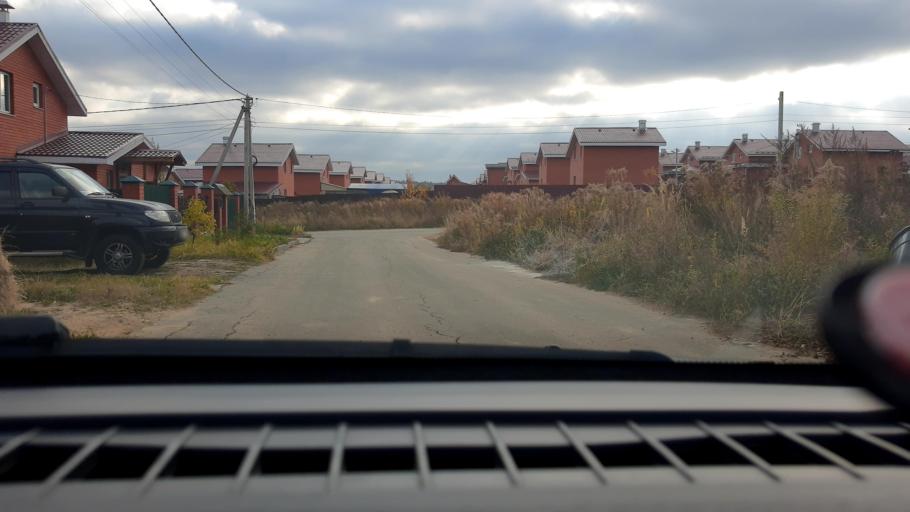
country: RU
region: Nizjnij Novgorod
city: Afonino
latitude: 56.1976
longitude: 44.0883
